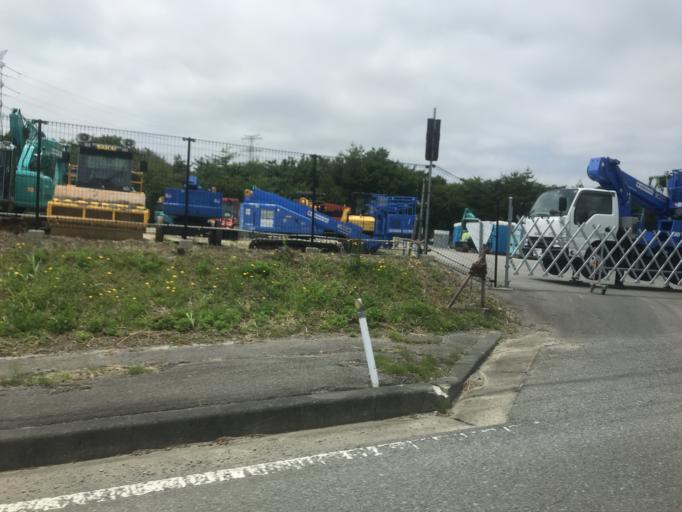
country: JP
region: Fukushima
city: Iwaki
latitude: 37.2439
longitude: 140.9917
